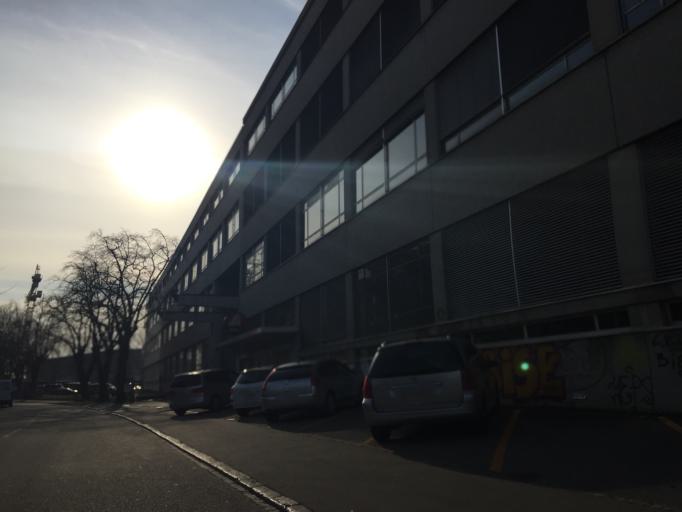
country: CH
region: Bern
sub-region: Bern-Mittelland District
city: Bern
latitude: 46.9628
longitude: 7.4495
